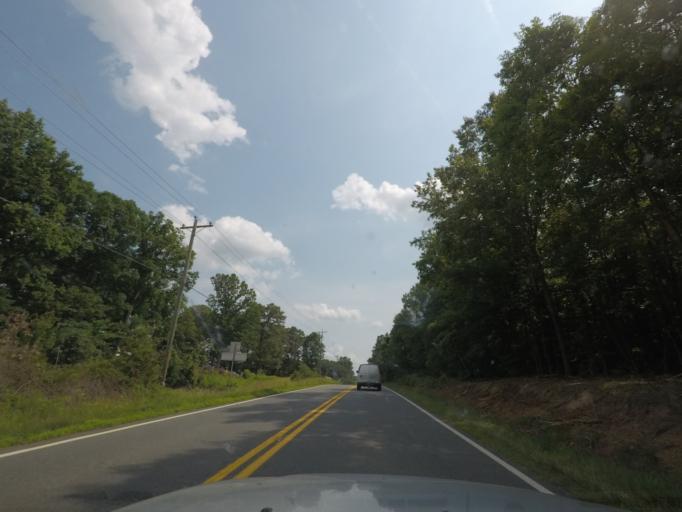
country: US
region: Virginia
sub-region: Fluvanna County
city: Palmyra
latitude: 37.9228
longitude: -78.2517
